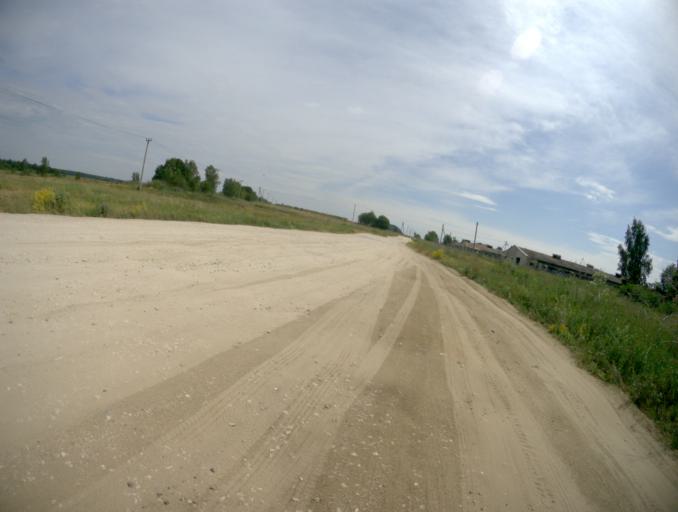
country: RU
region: Vladimir
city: Raduzhnyy
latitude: 56.0280
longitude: 40.3026
